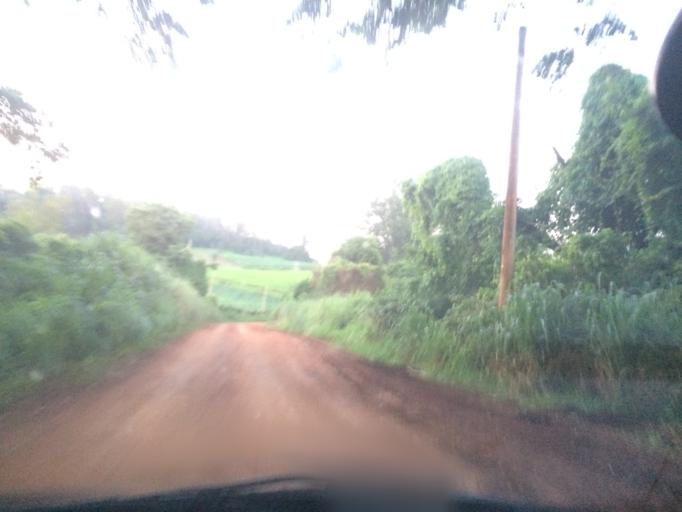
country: BR
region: Sao Paulo
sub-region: Tambau
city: Tambau
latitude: -21.7049
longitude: -47.2089
